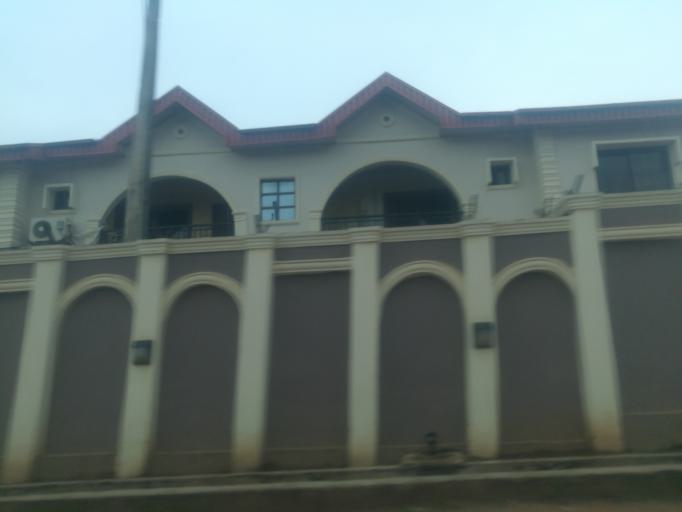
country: NG
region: Oyo
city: Ibadan
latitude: 7.3504
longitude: 3.8208
